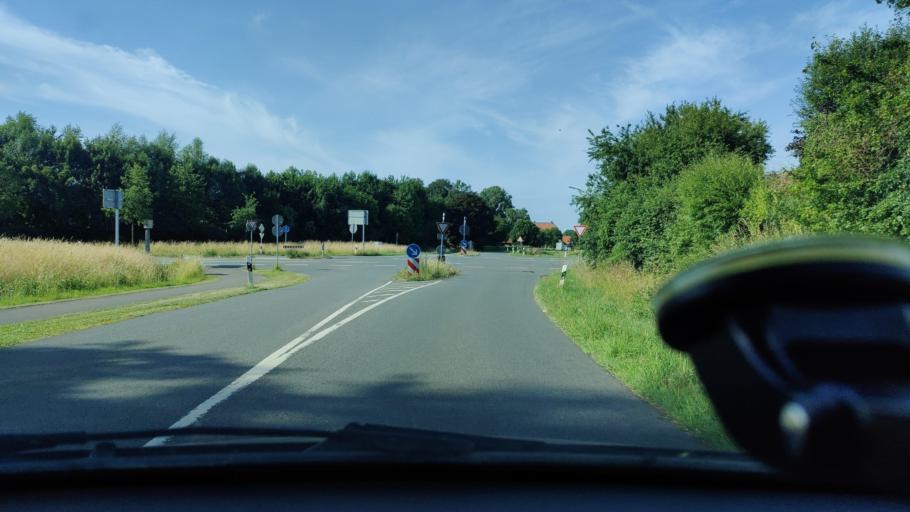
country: DE
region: North Rhine-Westphalia
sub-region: Regierungsbezirk Munster
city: Billerbeck
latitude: 52.0306
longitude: 7.2657
